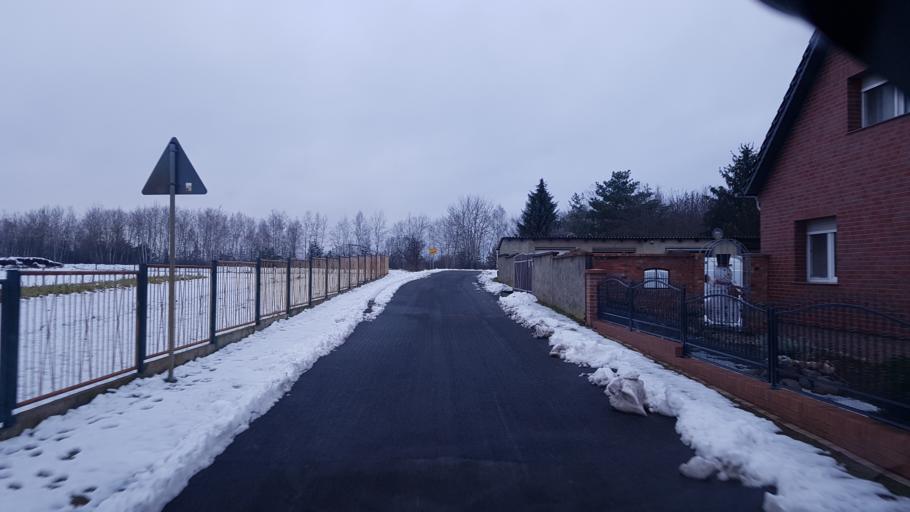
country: DE
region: Brandenburg
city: Vetschau
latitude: 51.7789
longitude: 14.0293
